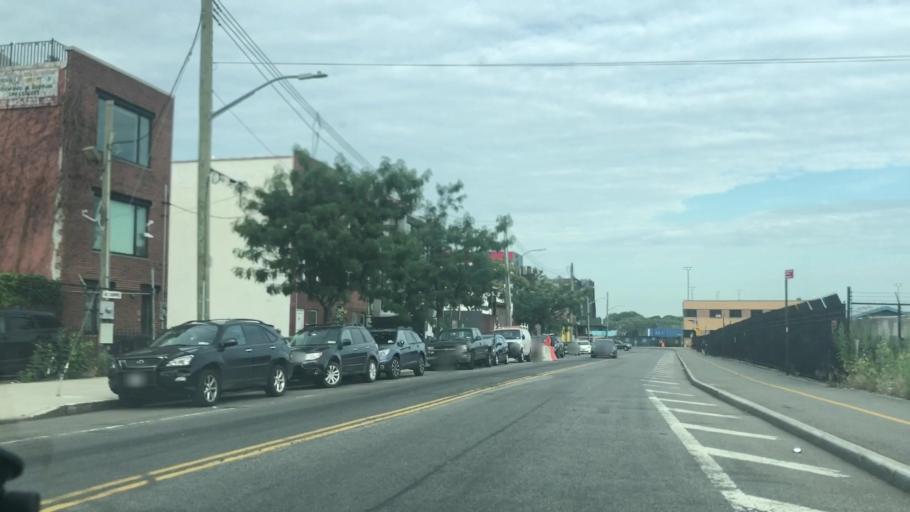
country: US
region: New York
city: New York City
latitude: 40.6858
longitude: -74.0025
